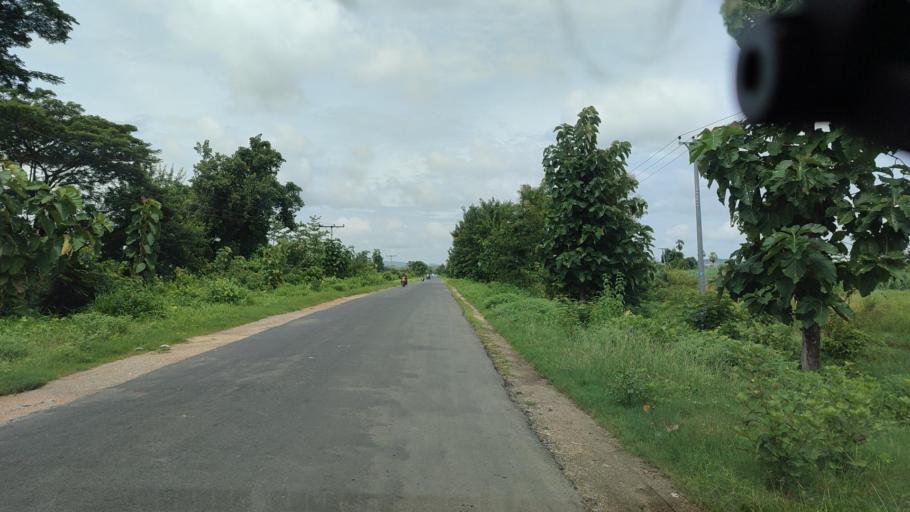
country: MM
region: Bago
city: Pyay
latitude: 18.8783
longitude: 95.2757
